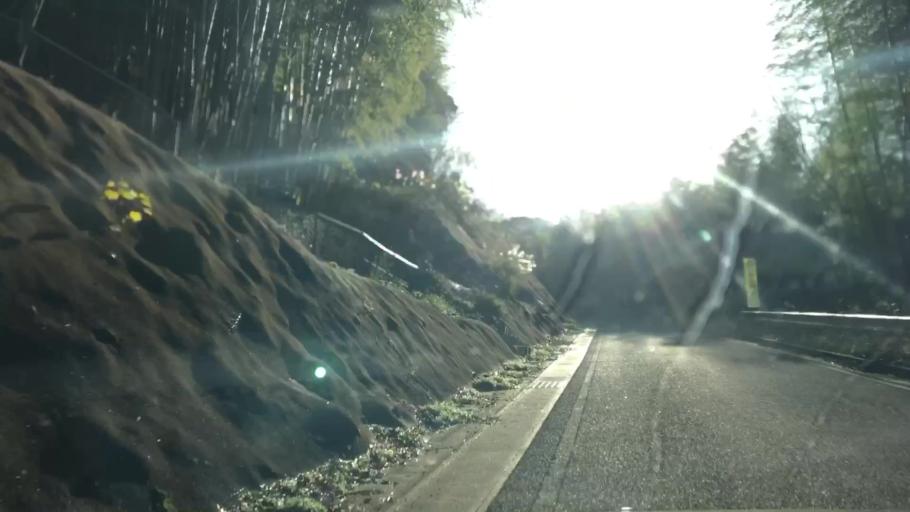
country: JP
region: Nagasaki
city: Sasebo
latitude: 33.0293
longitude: 129.6679
